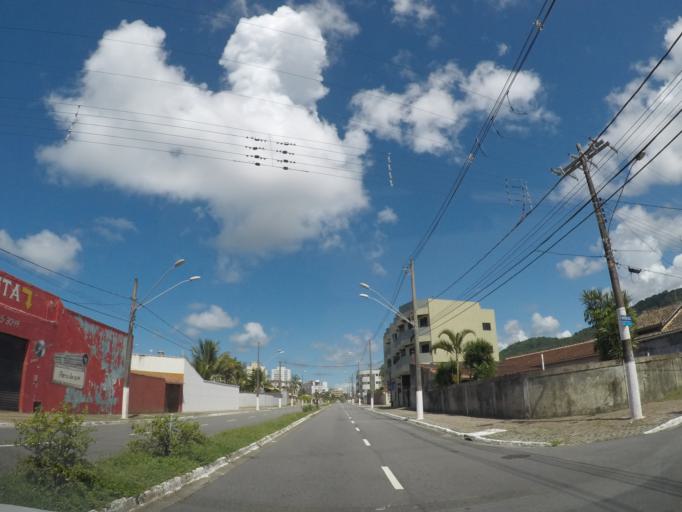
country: BR
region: Sao Paulo
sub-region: Mongagua
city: Mongagua
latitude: -24.0841
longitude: -46.5997
